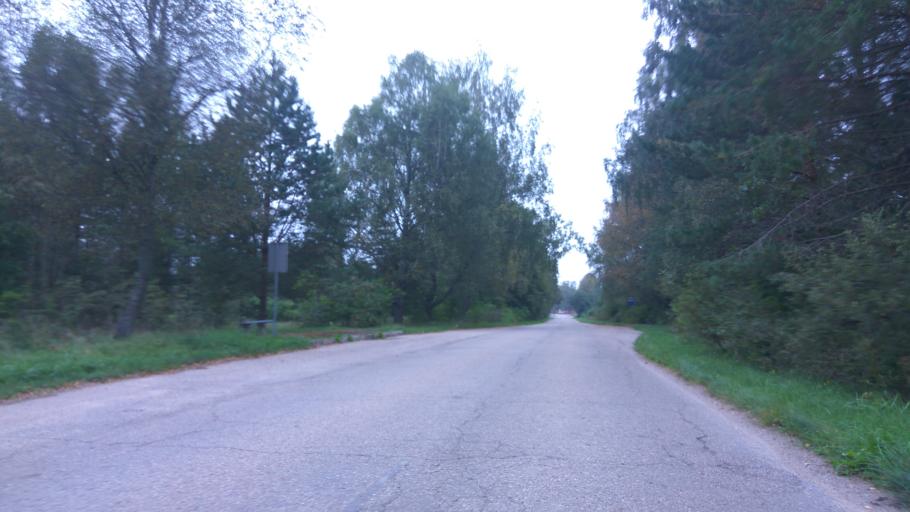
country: LV
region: Rucavas
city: Rucava
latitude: 56.1761
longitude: 21.1583
